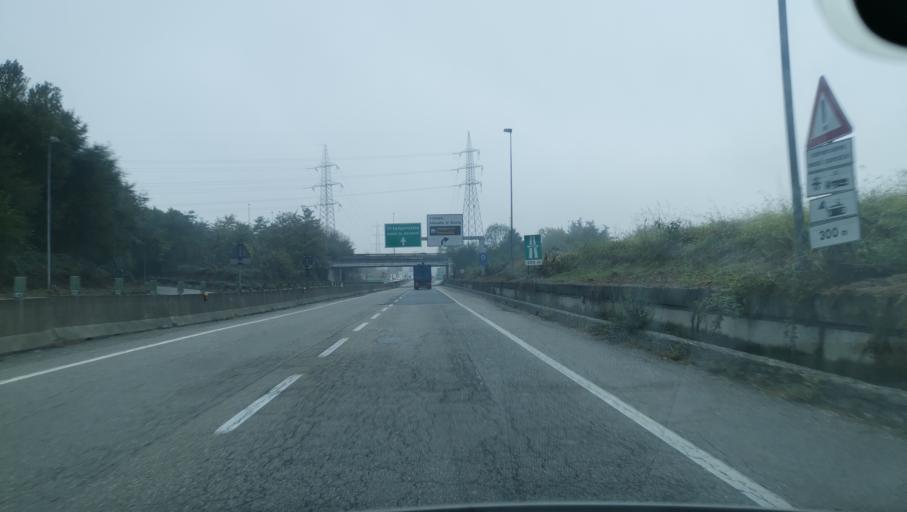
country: IT
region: Piedmont
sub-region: Provincia di Torino
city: San Mauro Torinese
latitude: 45.1148
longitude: 7.7360
